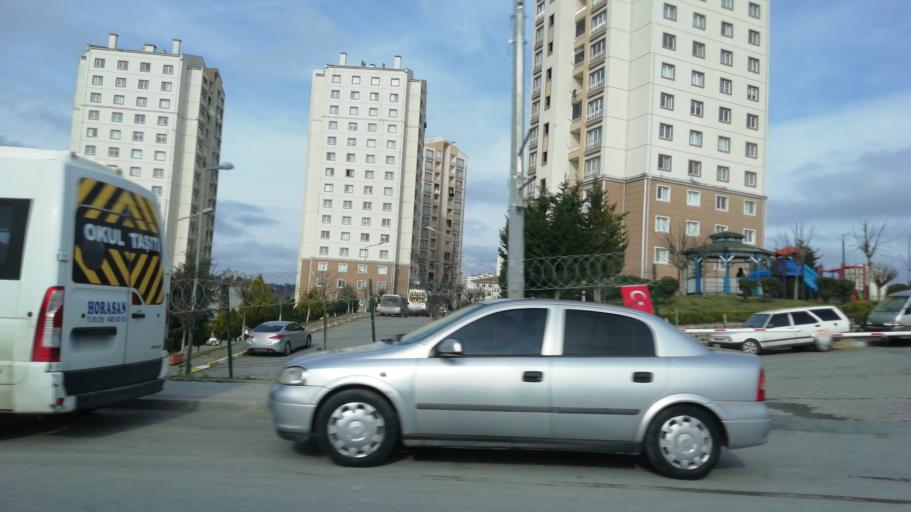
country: TR
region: Istanbul
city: Basaksehir
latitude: 41.1302
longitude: 28.7855
